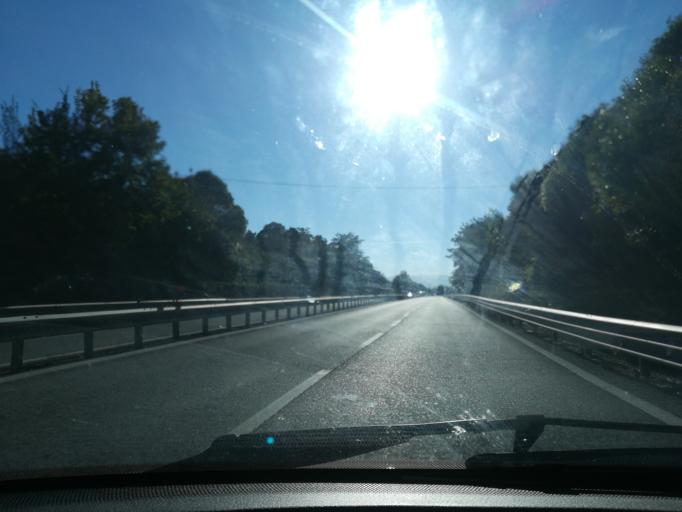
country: IT
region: The Marches
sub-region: Provincia di Macerata
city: Sforzacosta
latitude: 43.2467
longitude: 13.4279
